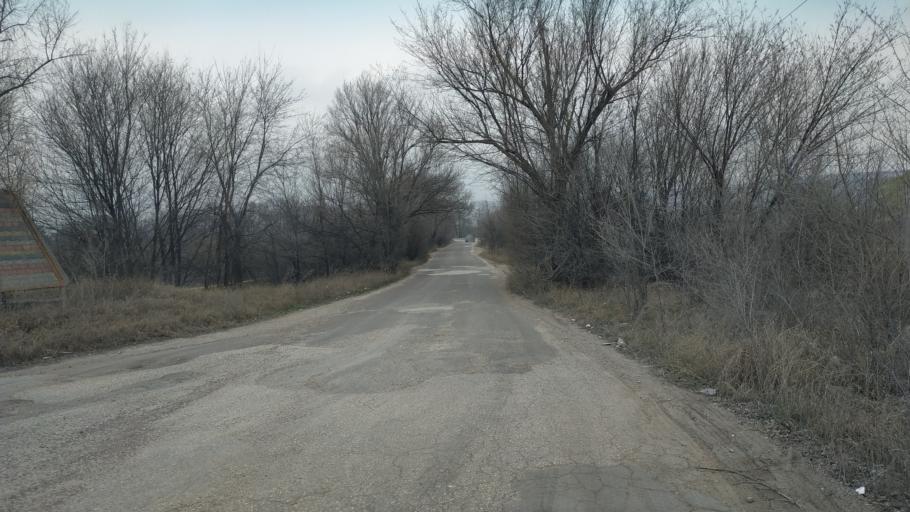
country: MD
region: Chisinau
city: Singera
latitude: 46.9237
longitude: 29.0040
